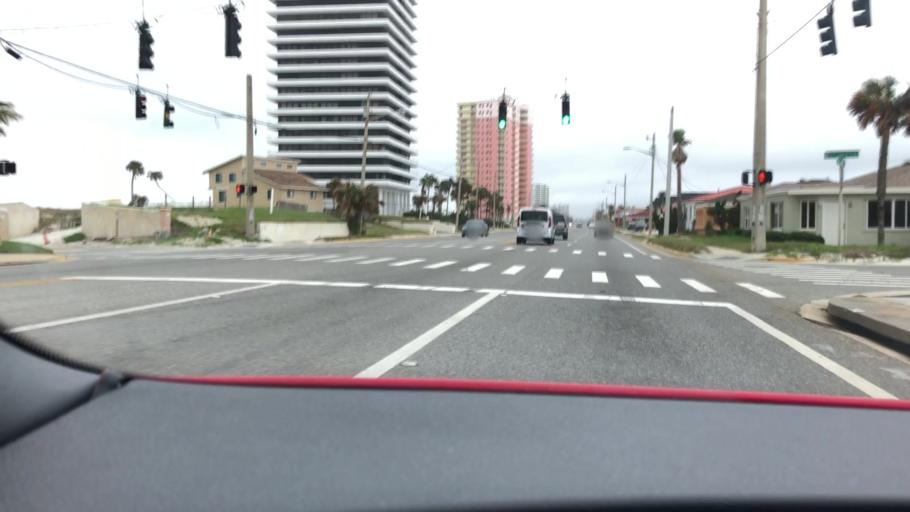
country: US
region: Florida
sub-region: Volusia County
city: Holly Hill
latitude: 29.2593
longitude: -81.0237
